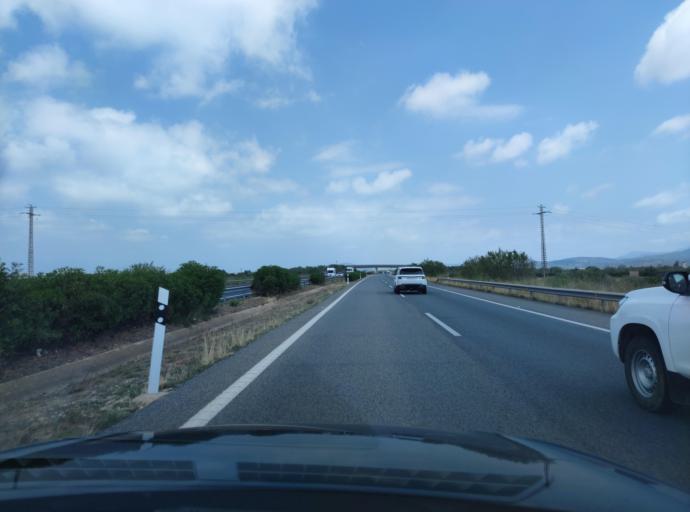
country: ES
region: Catalonia
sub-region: Provincia de Tarragona
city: Alcanar
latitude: 40.5216
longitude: 0.4165
